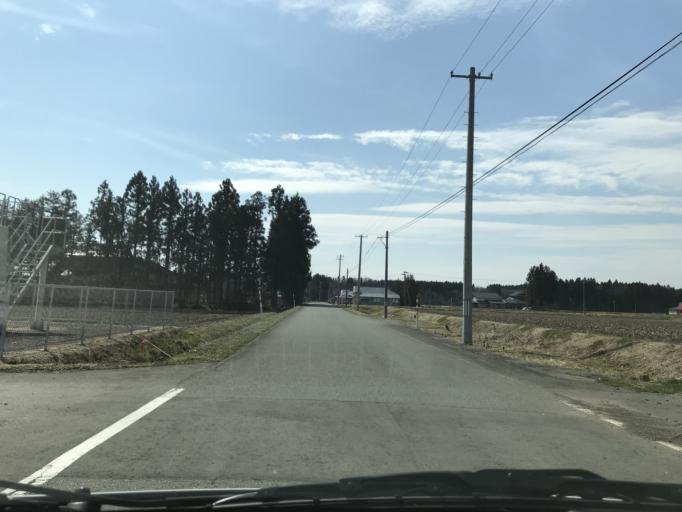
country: JP
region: Iwate
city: Mizusawa
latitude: 39.1239
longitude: 141.0433
